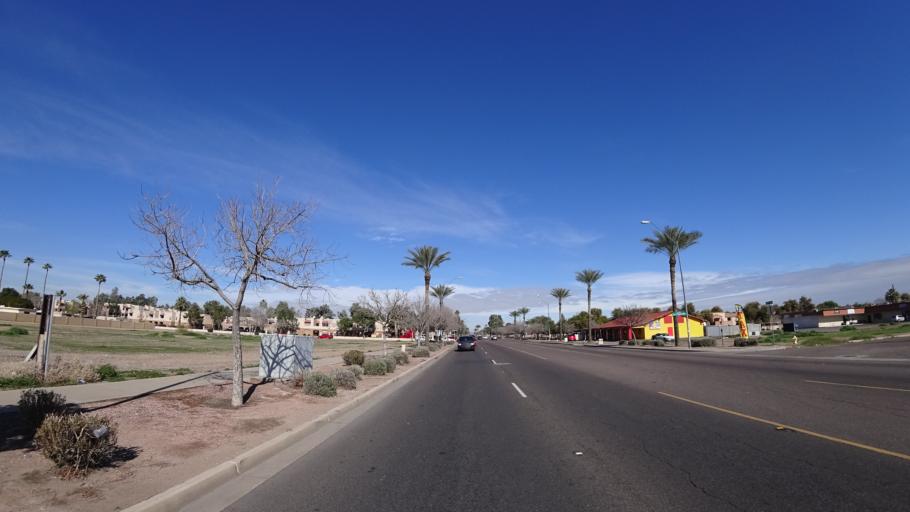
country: US
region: Arizona
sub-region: Maricopa County
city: Glendale
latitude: 33.5196
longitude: -112.1864
